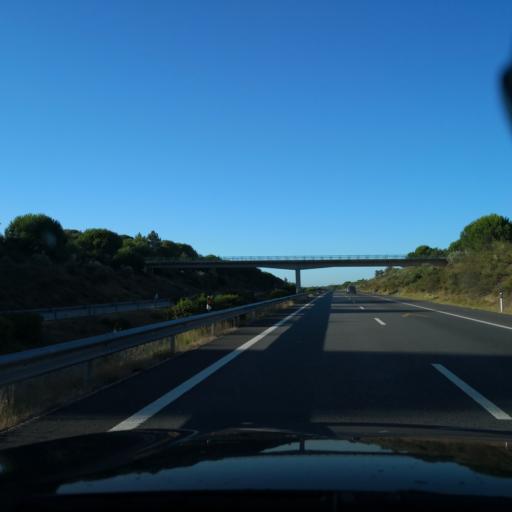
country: PT
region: Evora
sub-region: Vendas Novas
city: Vendas Novas
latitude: 38.5632
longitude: -8.6181
